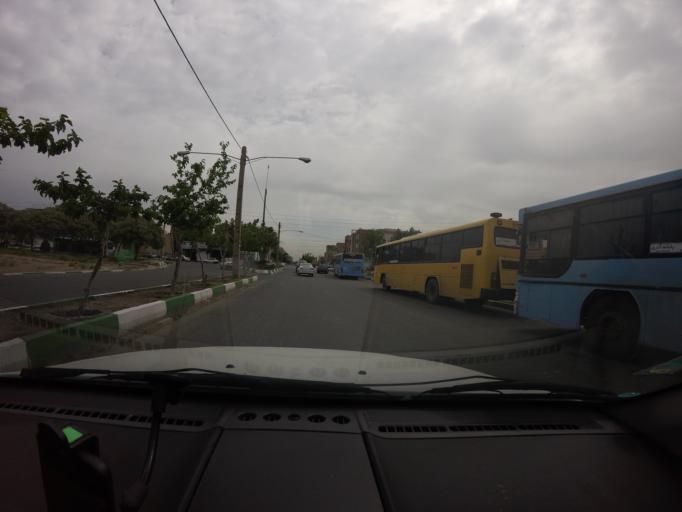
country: IR
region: Tehran
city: Eslamshahr
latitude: 35.5459
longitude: 51.2412
